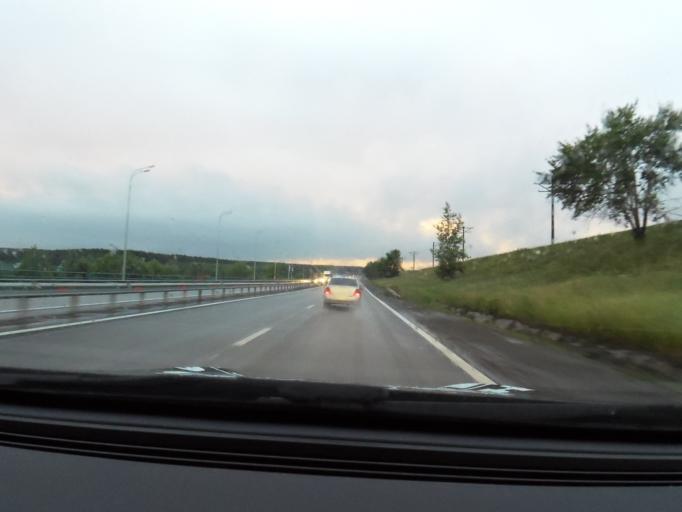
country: RU
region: Tatarstan
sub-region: Tukayevskiy Rayon
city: Naberezhnyye Chelny
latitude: 55.7124
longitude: 52.2711
